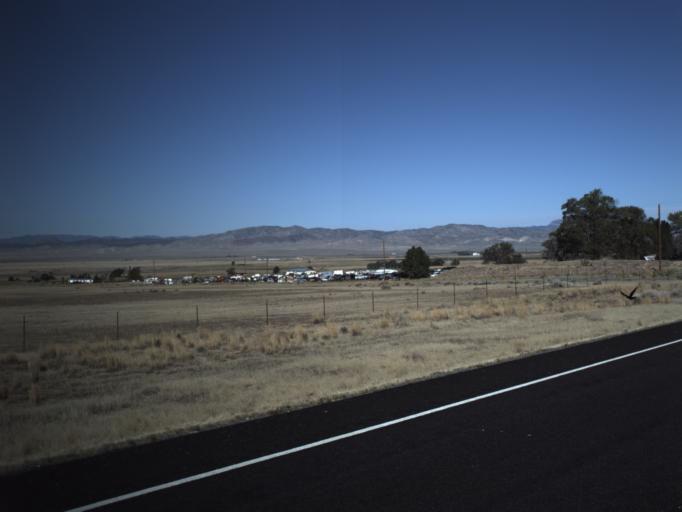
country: US
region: Utah
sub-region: Beaver County
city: Milford
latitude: 38.2607
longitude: -112.9522
